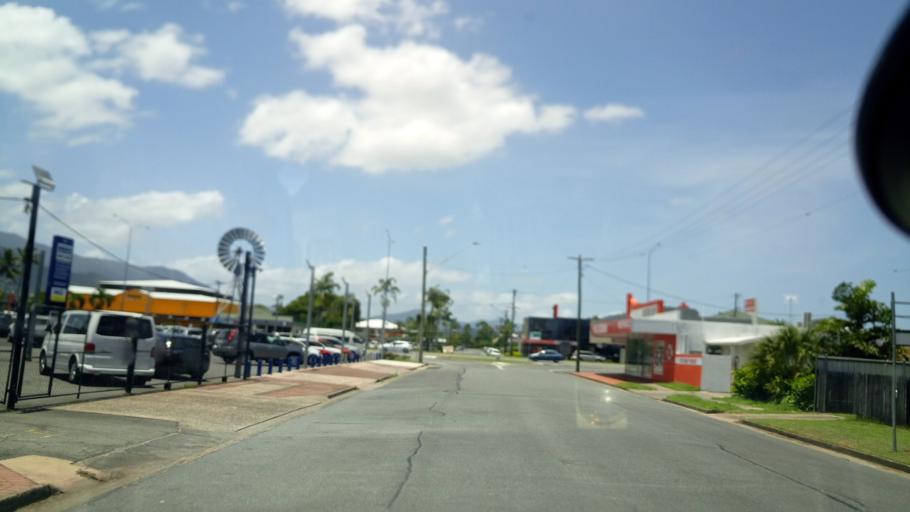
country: AU
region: Queensland
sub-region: Cairns
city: Cairns
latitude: -16.9348
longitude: 145.7565
